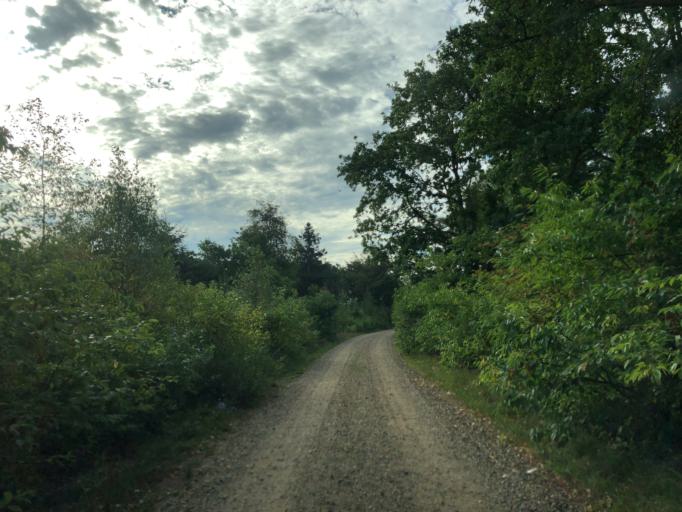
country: DK
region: Central Jutland
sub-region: Holstebro Kommune
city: Ulfborg
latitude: 56.1850
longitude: 8.3461
